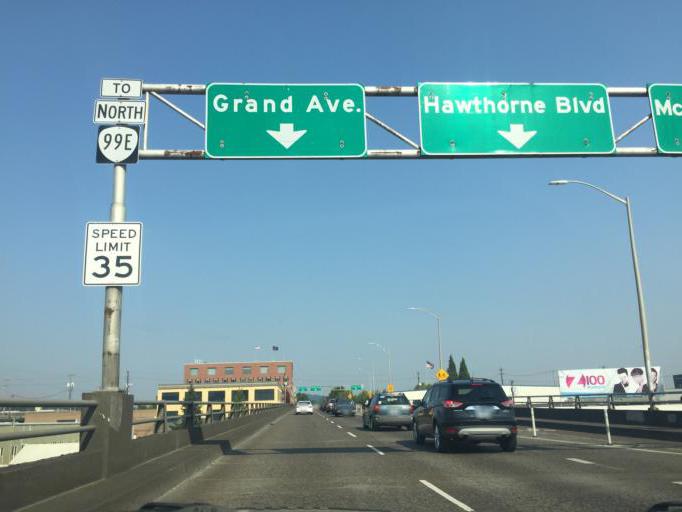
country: US
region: Oregon
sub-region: Multnomah County
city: Portland
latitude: 45.5123
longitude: -122.6647
